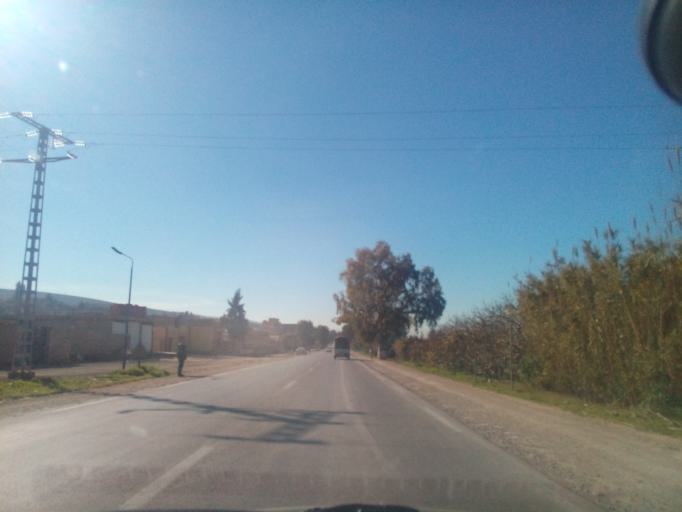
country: DZ
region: Chlef
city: Boukadir
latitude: 36.0167
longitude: 1.0318
